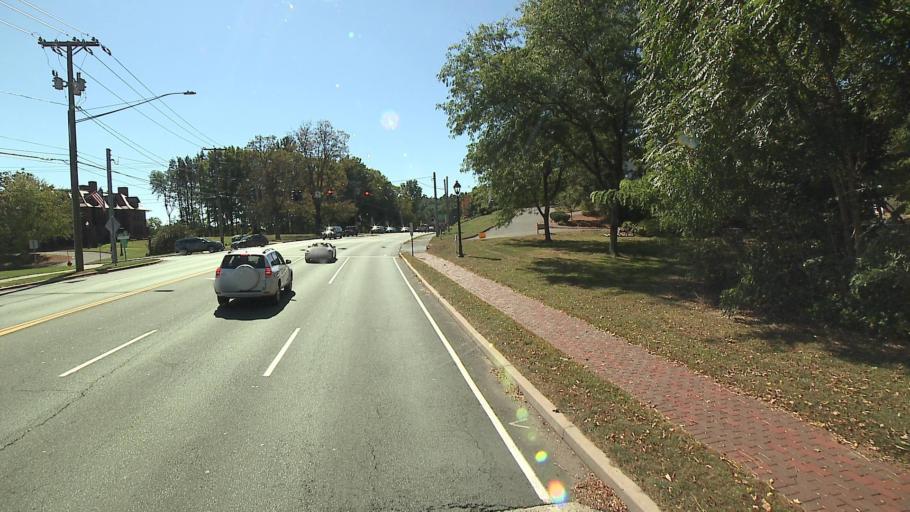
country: US
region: Connecticut
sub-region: Hartford County
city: Simsbury Center
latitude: 41.8713
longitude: -72.8035
